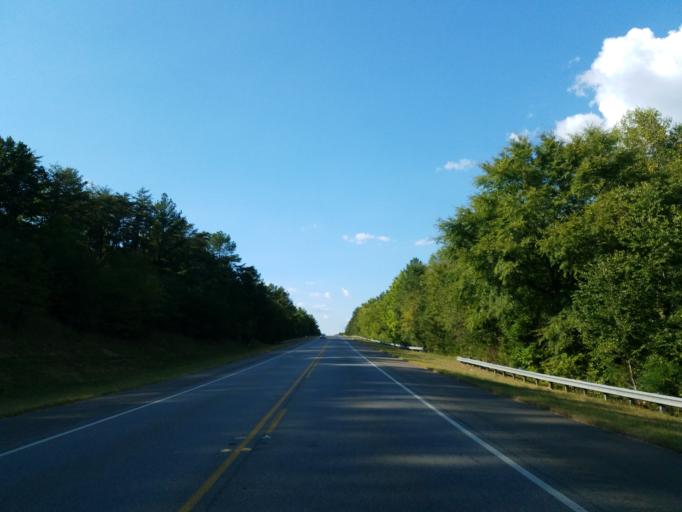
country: US
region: Georgia
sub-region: Murray County
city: Chatsworth
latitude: 34.6790
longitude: -84.7272
